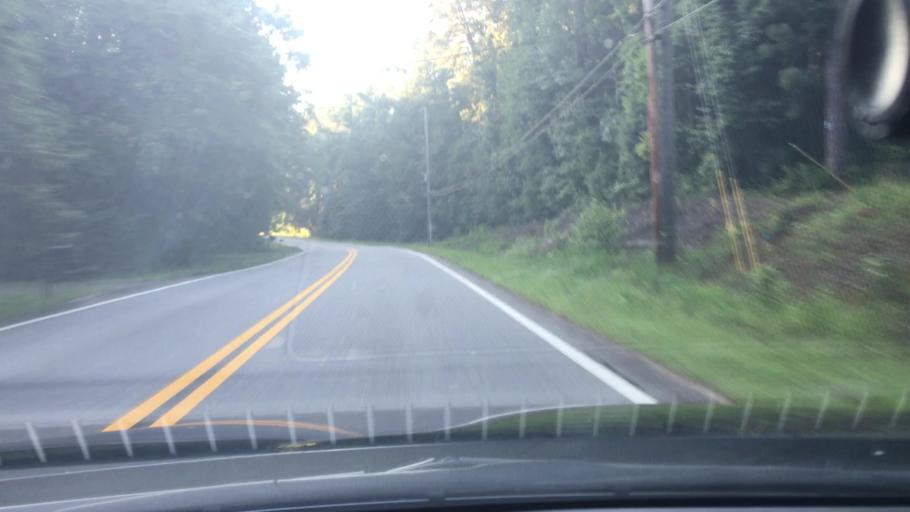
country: US
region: Georgia
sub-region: Coweta County
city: East Newnan
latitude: 33.3411
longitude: -84.7411
